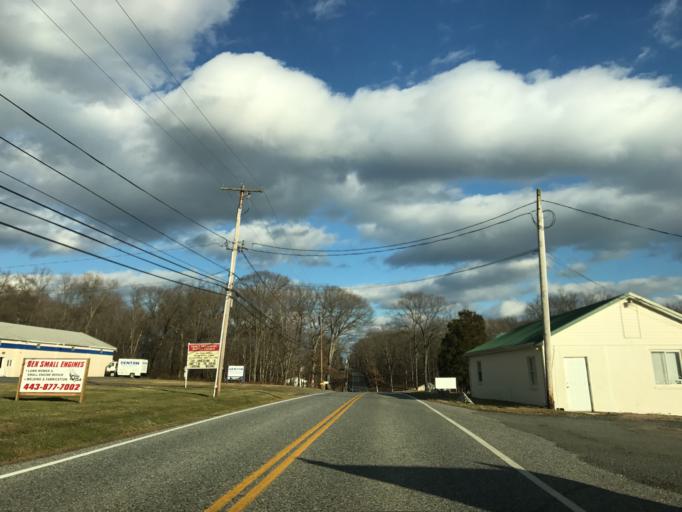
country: US
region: Maryland
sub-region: Cecil County
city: North East
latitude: 39.6435
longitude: -75.9711
